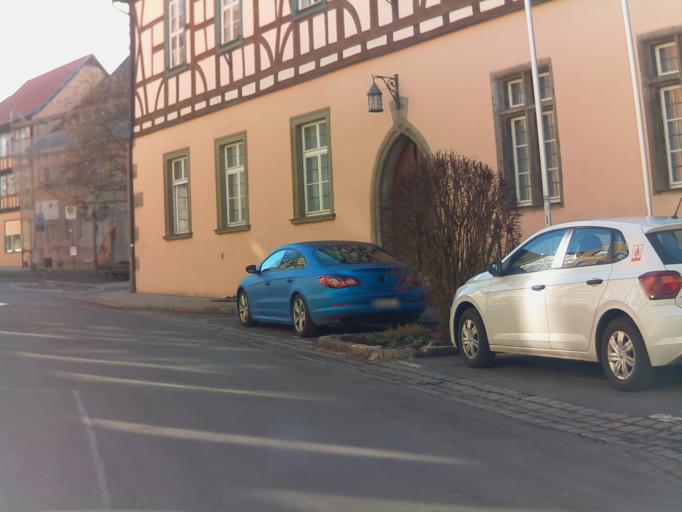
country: DE
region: Bavaria
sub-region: Regierungsbezirk Unterfranken
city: Munnerstadt
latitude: 50.2491
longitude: 10.1947
